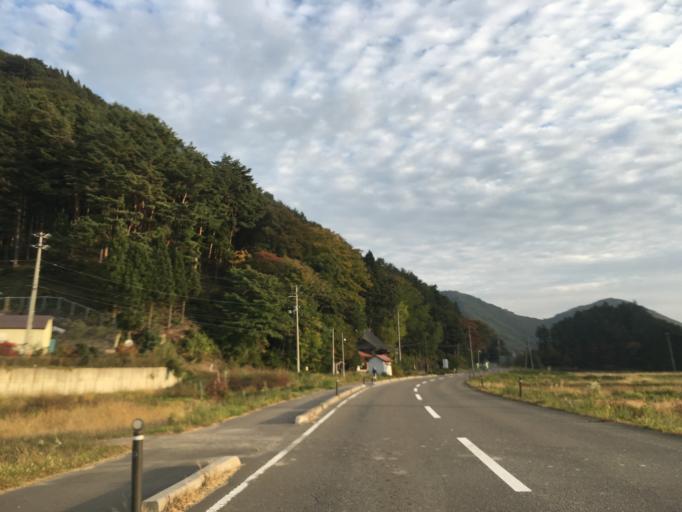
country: JP
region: Fukushima
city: Inawashiro
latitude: 37.5088
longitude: 140.1459
